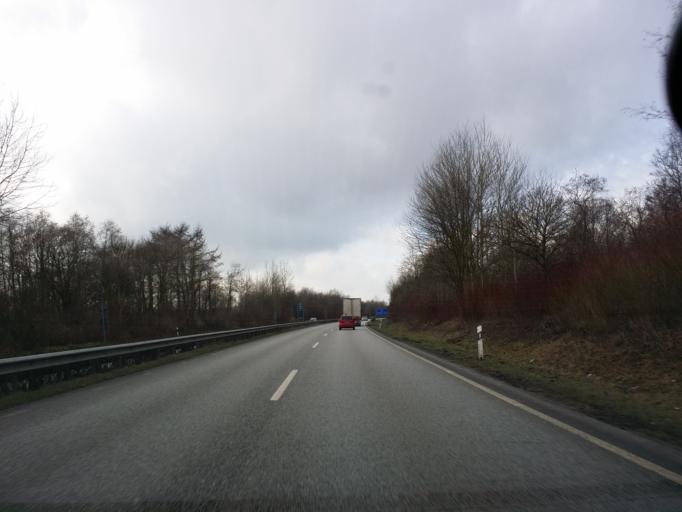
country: DE
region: Schleswig-Holstein
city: Melsdorf
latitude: 54.3074
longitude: 10.0230
